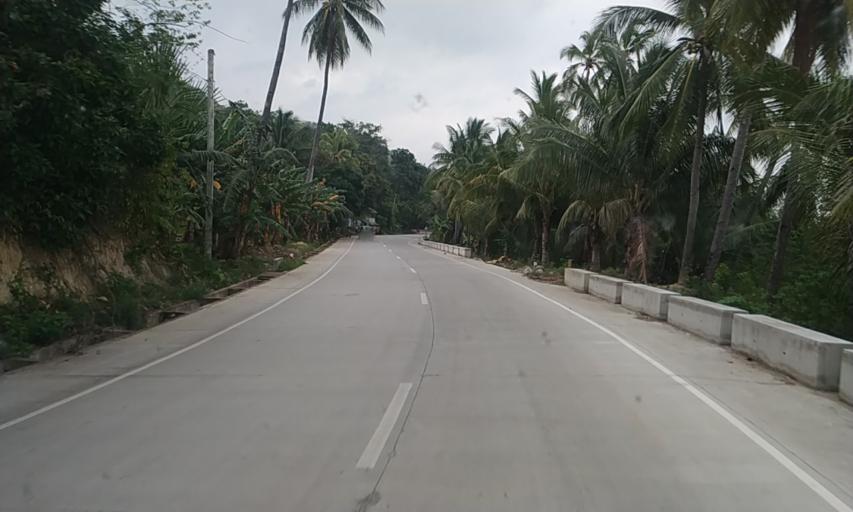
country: PH
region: Central Visayas
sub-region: Province of Negros Oriental
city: Basak
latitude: 10.2015
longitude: 123.2994
